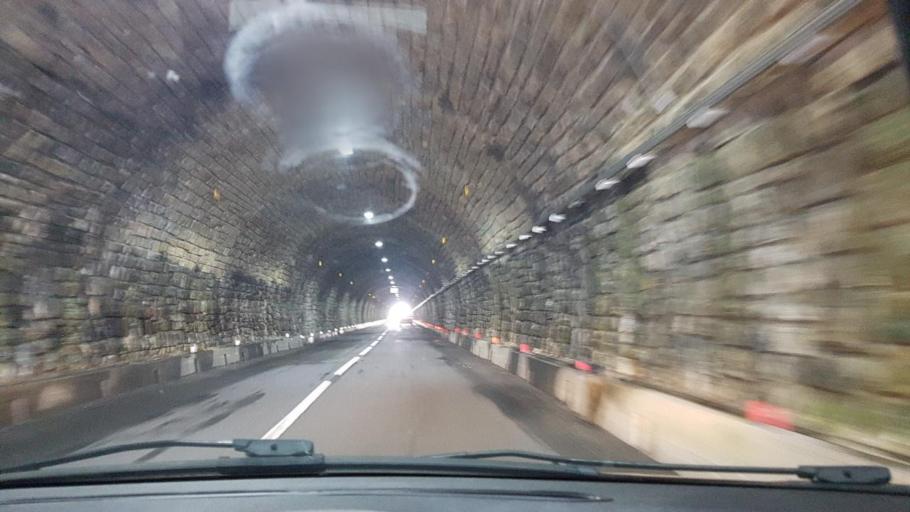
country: AT
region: Carinthia
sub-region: Politischer Bezirk Spittal an der Drau
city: Heiligenblut
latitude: 47.0814
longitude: 12.8427
